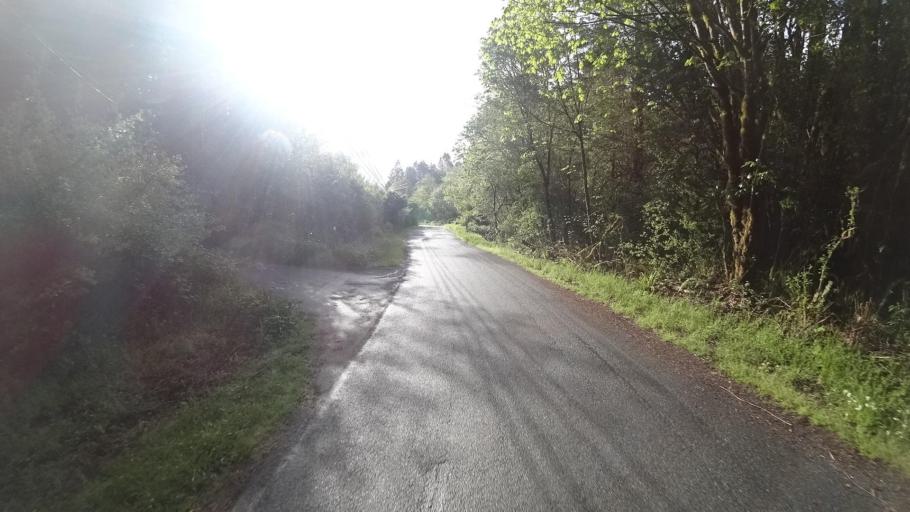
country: US
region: California
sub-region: Humboldt County
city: Blue Lake
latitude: 40.8823
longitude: -124.0205
